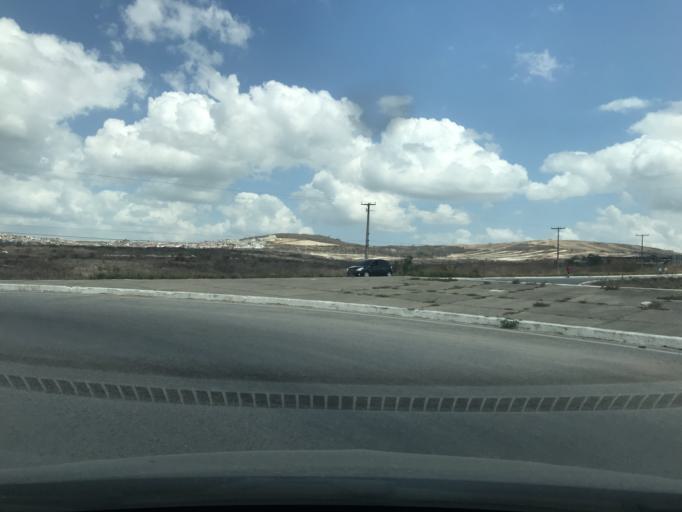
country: BR
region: Pernambuco
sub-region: Caruaru
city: Caruaru
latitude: -8.3042
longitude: -35.9889
